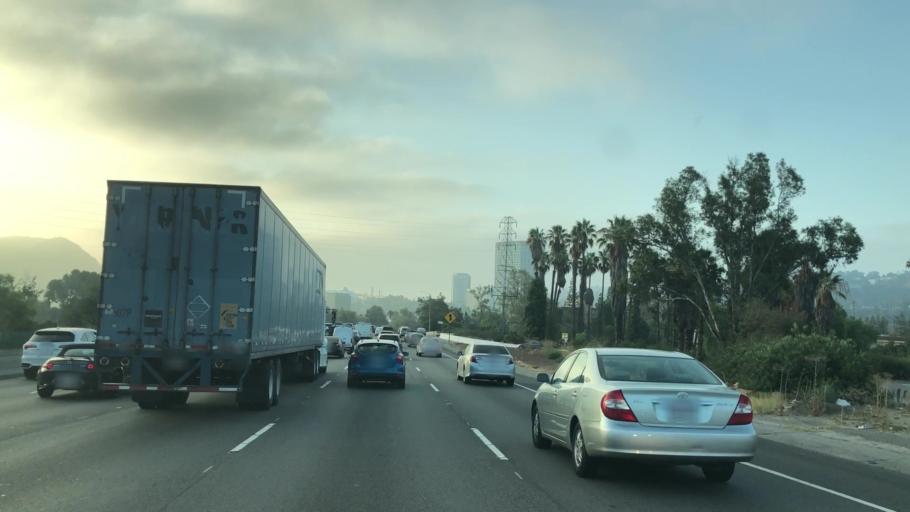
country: US
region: California
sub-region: Los Angeles County
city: Universal City
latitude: 34.1478
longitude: -118.3720
